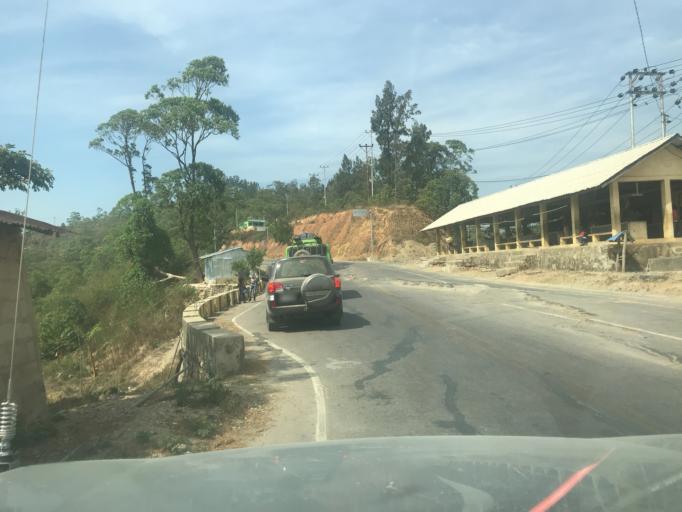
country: TL
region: Aileu
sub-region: Aileu Villa
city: Aileu
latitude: -8.6846
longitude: 125.5478
